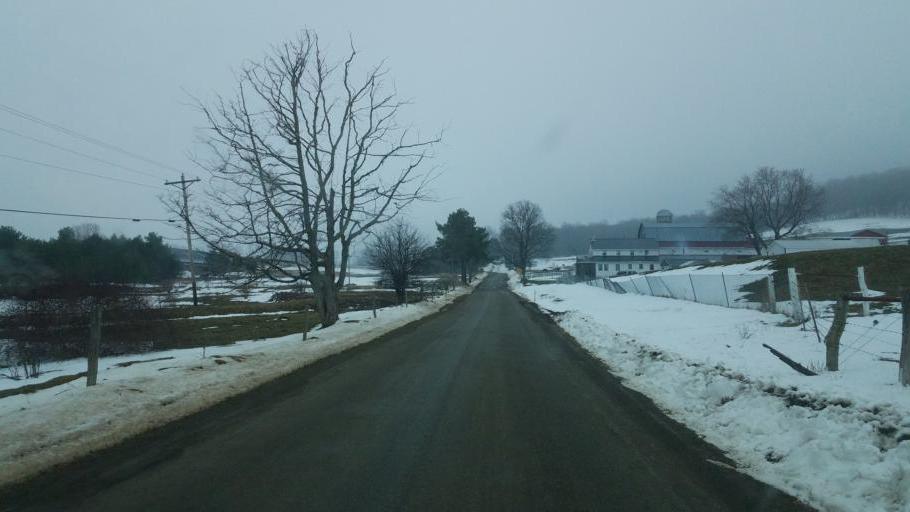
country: US
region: New York
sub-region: Allegany County
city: Andover
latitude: 41.9833
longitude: -77.7617
